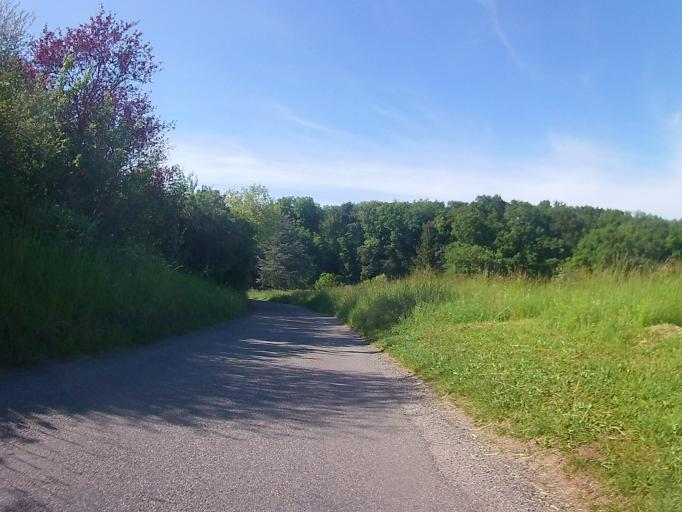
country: DE
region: Baden-Wuerttemberg
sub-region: Regierungsbezirk Stuttgart
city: Fellbach
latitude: 48.7825
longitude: 9.2890
